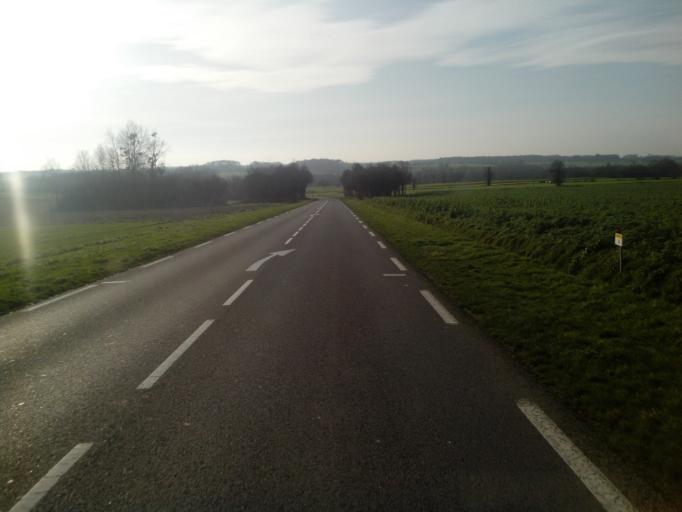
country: FR
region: Brittany
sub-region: Departement d'Ille-et-Vilaine
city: Gael
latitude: 48.1383
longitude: -2.2243
